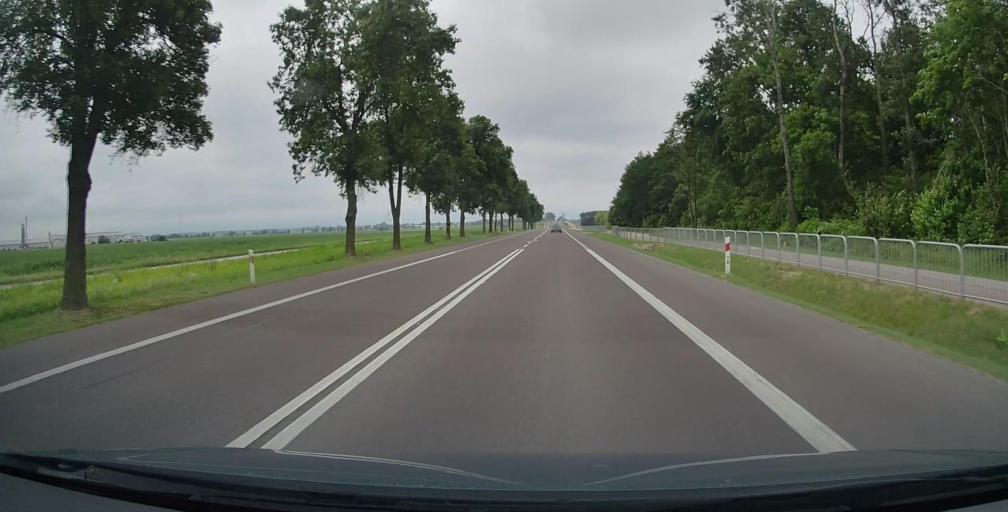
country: PL
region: Lublin Voivodeship
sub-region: Powiat bialski
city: Miedzyrzec Podlaski
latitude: 52.0090
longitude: 22.7433
